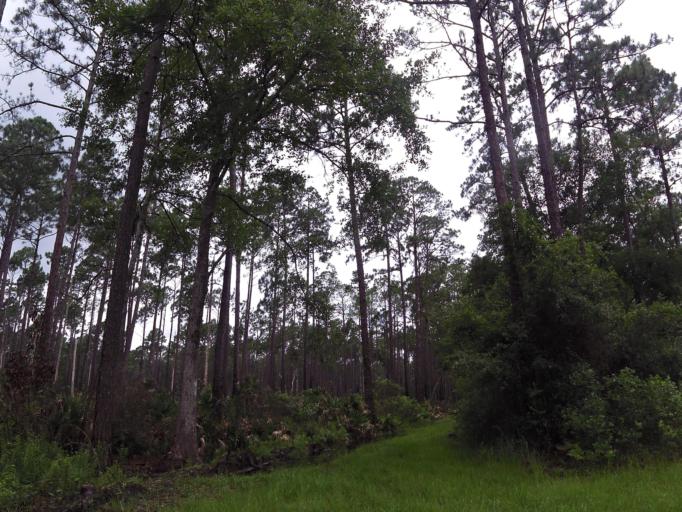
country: US
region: Florida
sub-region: Clay County
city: Green Cove Springs
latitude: 29.9732
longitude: -81.6391
